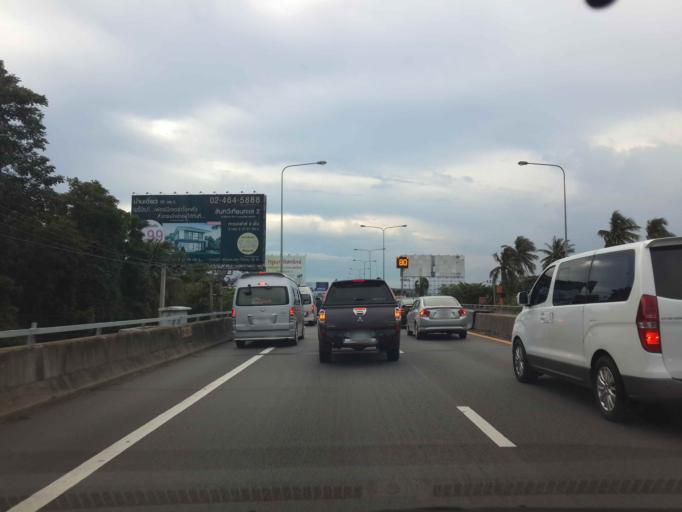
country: TH
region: Bangkok
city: Chom Thong
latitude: 13.6720
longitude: 100.4910
